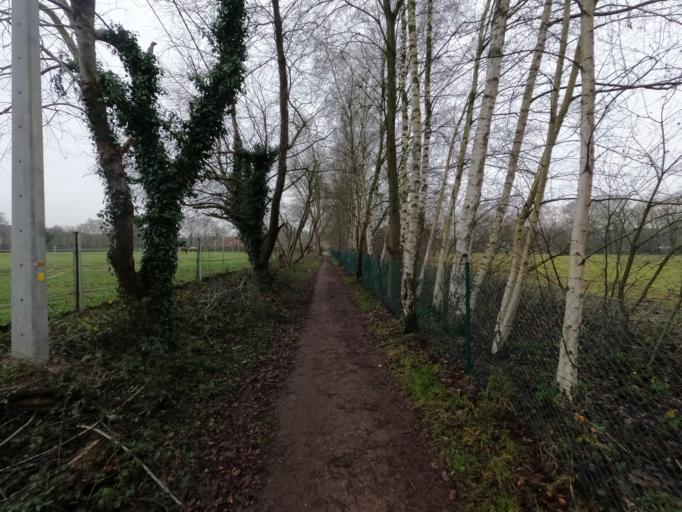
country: BE
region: Flanders
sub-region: Provincie Antwerpen
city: Schilde
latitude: 51.2895
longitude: 4.5825
